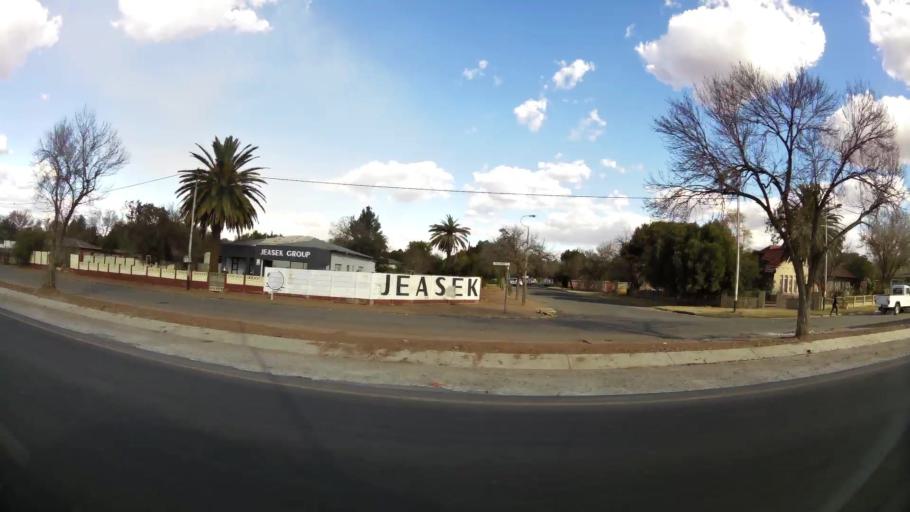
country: ZA
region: North-West
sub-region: Dr Kenneth Kaunda District Municipality
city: Klerksdorp
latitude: -26.8651
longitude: 26.6432
